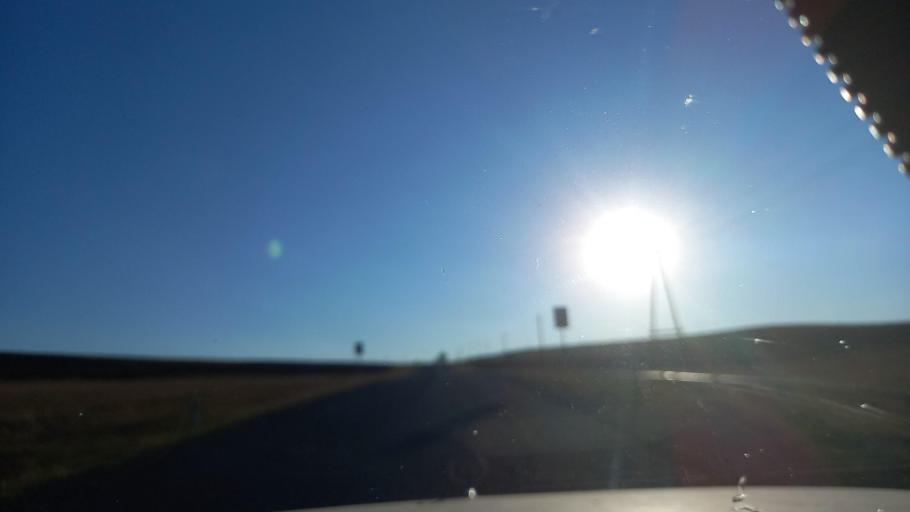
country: AZ
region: Shamkir Rayon
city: Shamkhor
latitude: 40.7603
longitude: 45.9137
